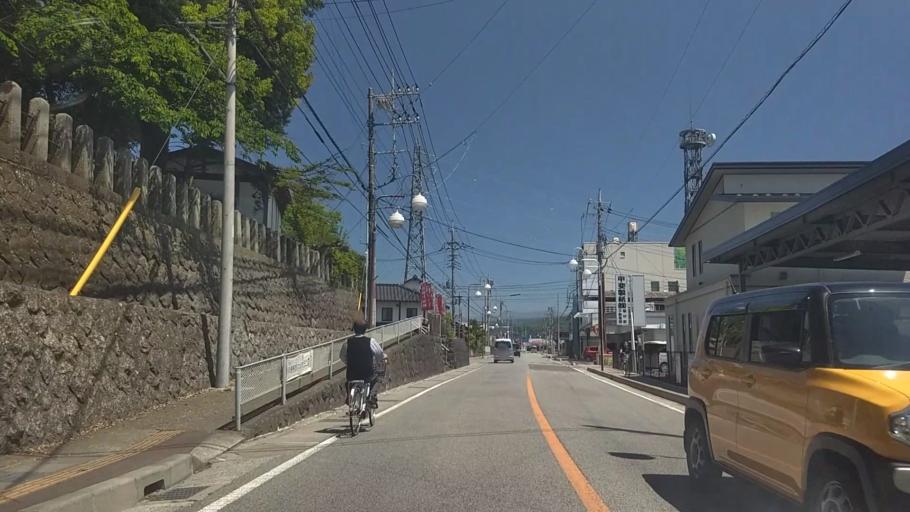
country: JP
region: Yamanashi
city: Nirasaki
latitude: 35.7142
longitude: 138.4481
